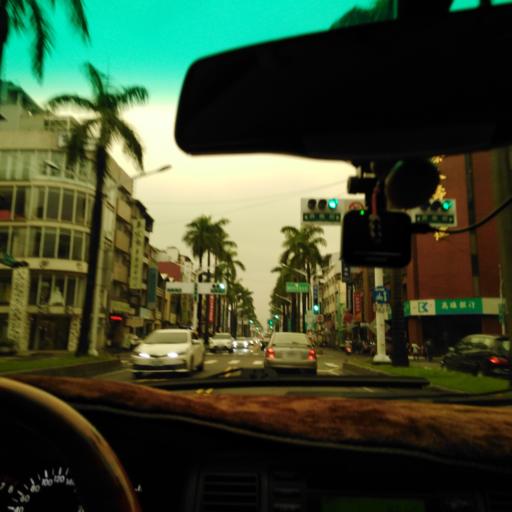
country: TW
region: Taiwan
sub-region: Pingtung
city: Pingtung
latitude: 22.6769
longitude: 120.4902
